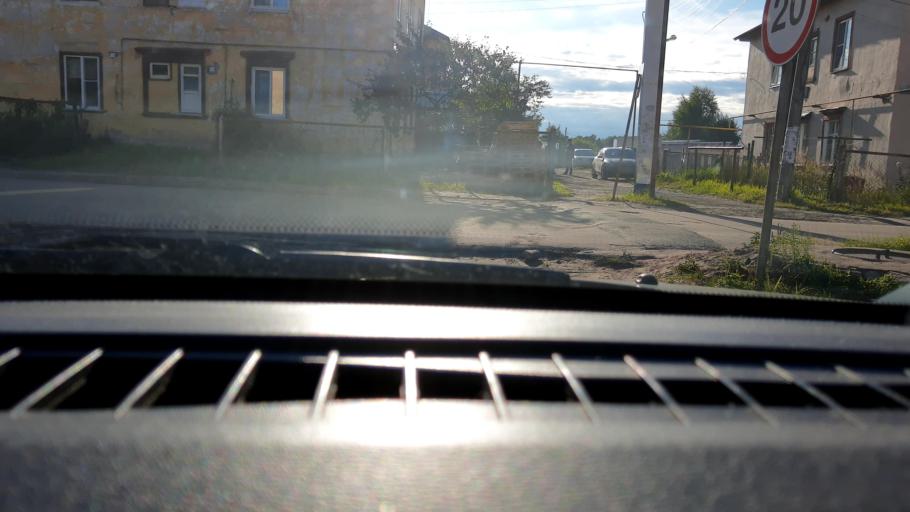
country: RU
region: Nizjnij Novgorod
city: Lukino
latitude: 56.3362
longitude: 43.6179
